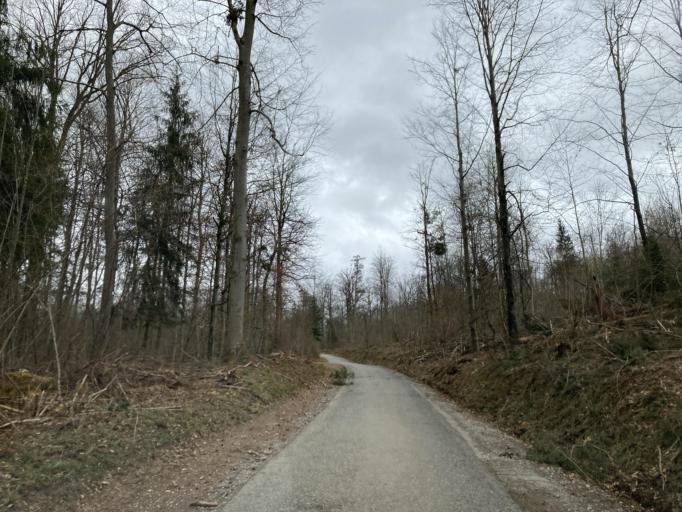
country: DE
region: Baden-Wuerttemberg
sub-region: Tuebingen Region
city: Gomaringen
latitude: 48.4907
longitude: 9.0801
